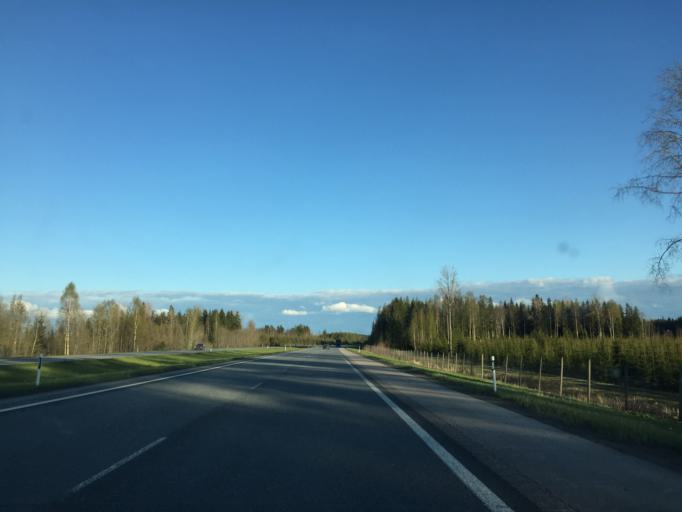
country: FI
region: Haeme
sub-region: Haemeenlinna
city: Tervakoski
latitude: 60.7842
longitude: 24.7037
